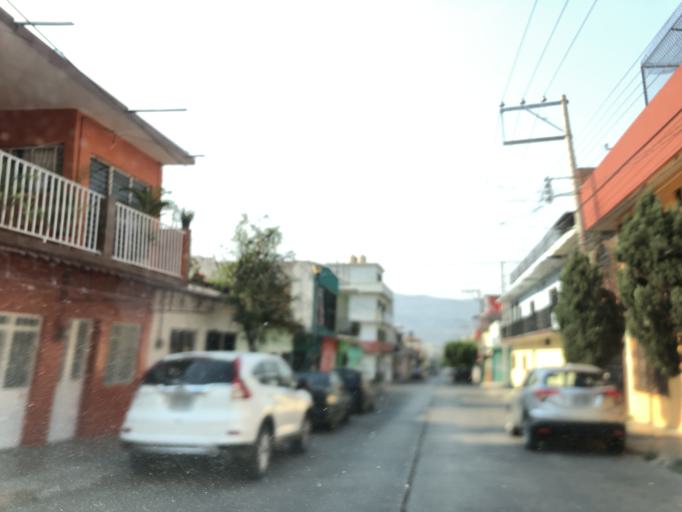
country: MX
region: Chiapas
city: Tuxtla Gutierrez
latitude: 16.7481
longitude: -93.1224
